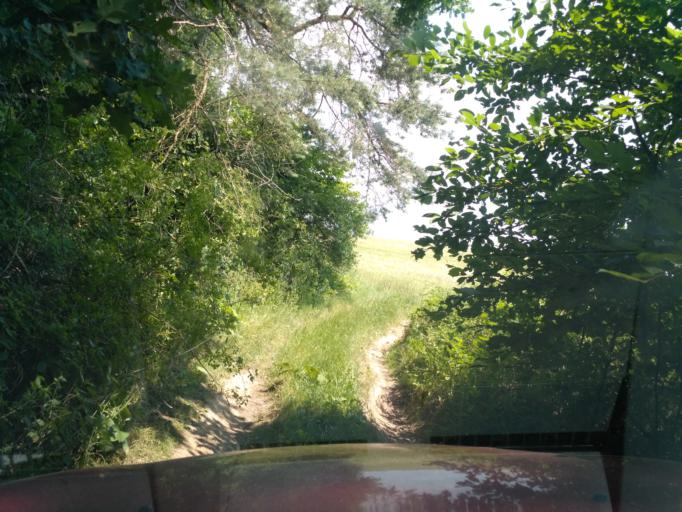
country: SK
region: Kosicky
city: Moldava nad Bodvou
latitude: 48.6220
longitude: 21.0470
